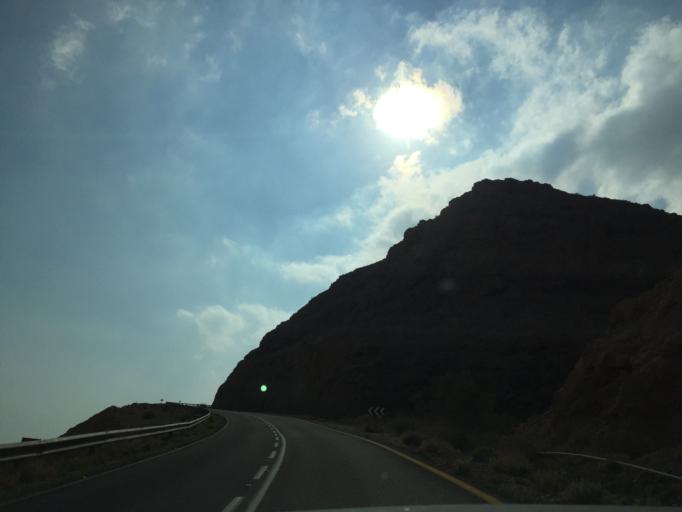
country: IL
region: Southern District
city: `En Boqeq
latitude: 31.3218
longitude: 35.3326
